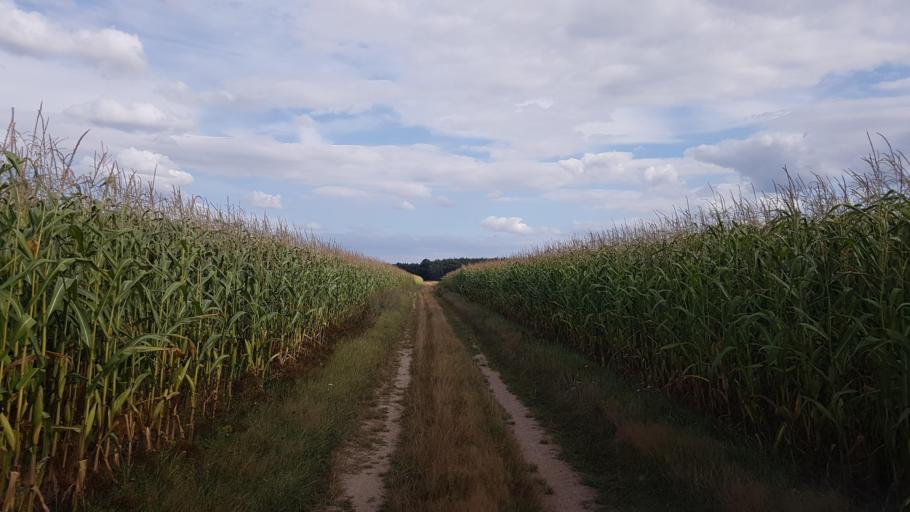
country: DE
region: Brandenburg
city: Bad Liebenwerda
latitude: 51.5084
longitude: 13.3023
